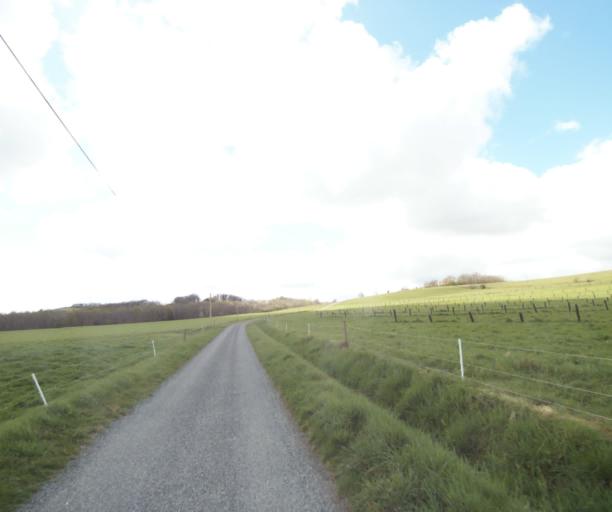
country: FR
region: Midi-Pyrenees
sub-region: Departement de l'Ariege
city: Saverdun
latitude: 43.1927
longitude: 1.5826
